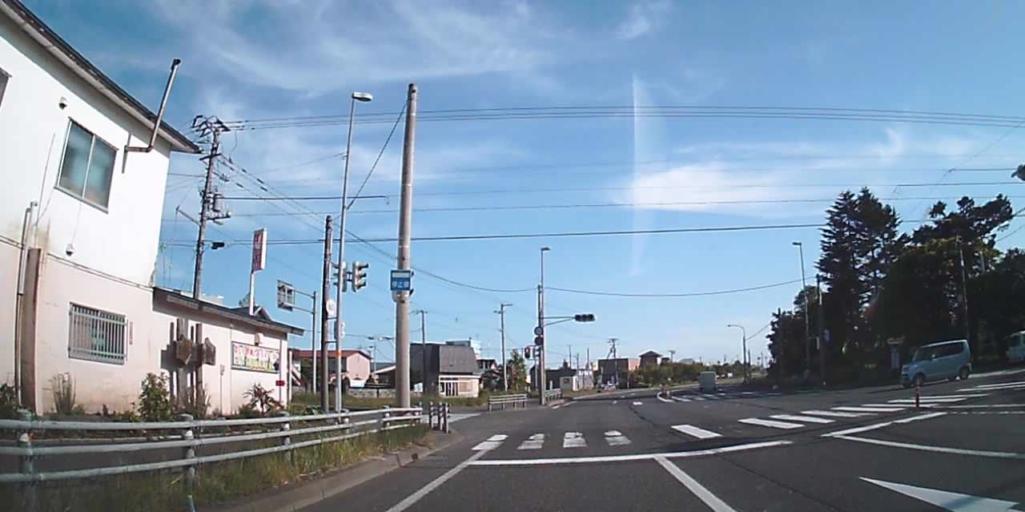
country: JP
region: Hokkaido
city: Shiraoi
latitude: 42.4516
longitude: 141.1759
